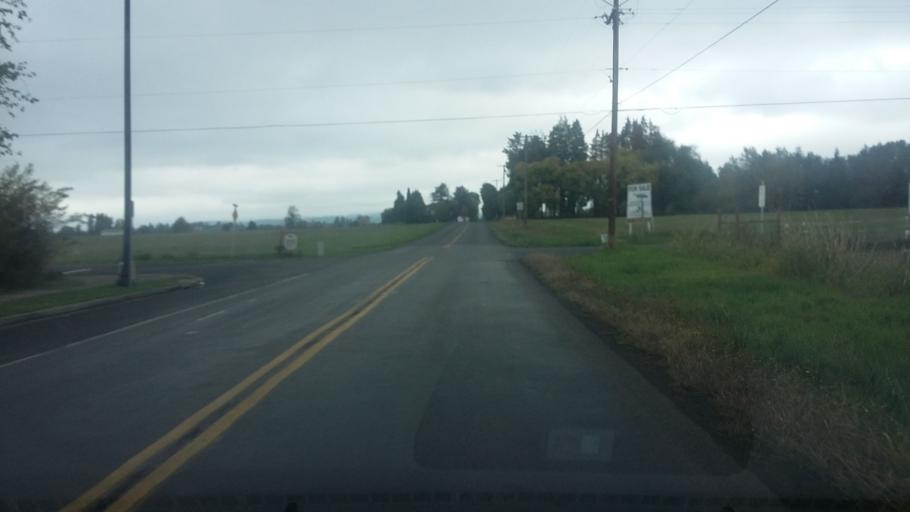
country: US
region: Washington
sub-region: Clark County
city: La Center
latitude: 45.8226
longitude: -122.6826
